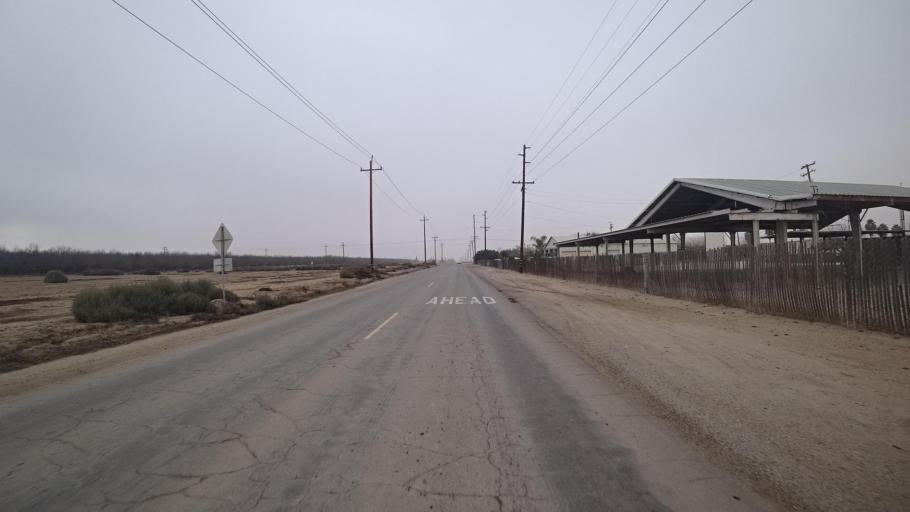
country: US
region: California
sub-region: Kern County
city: Greenfield
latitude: 35.0947
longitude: -119.1079
